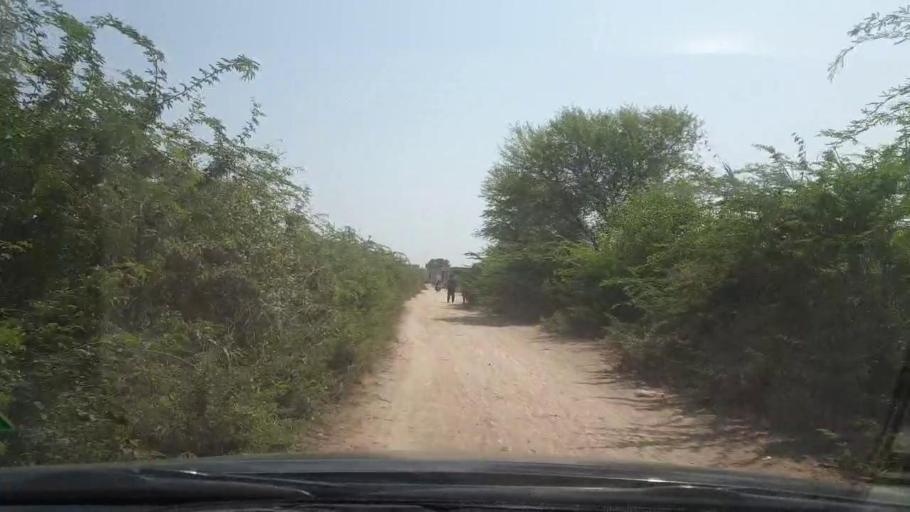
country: PK
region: Sindh
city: Naukot
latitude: 24.7679
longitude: 69.1958
